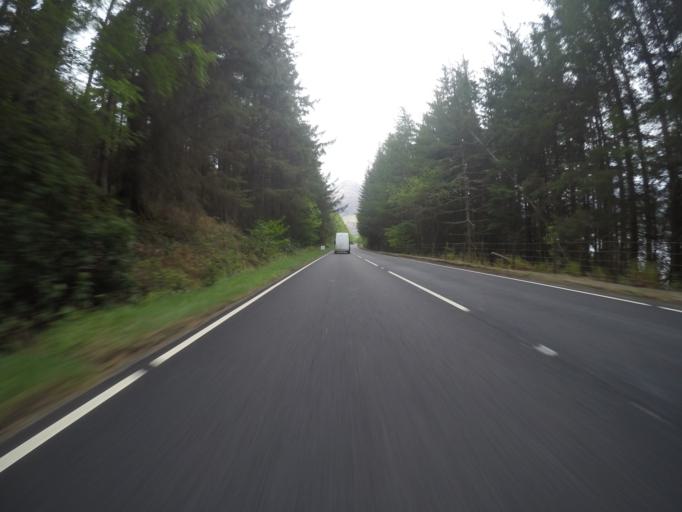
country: GB
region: Scotland
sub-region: Highland
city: Fort William
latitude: 57.2382
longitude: -5.4400
